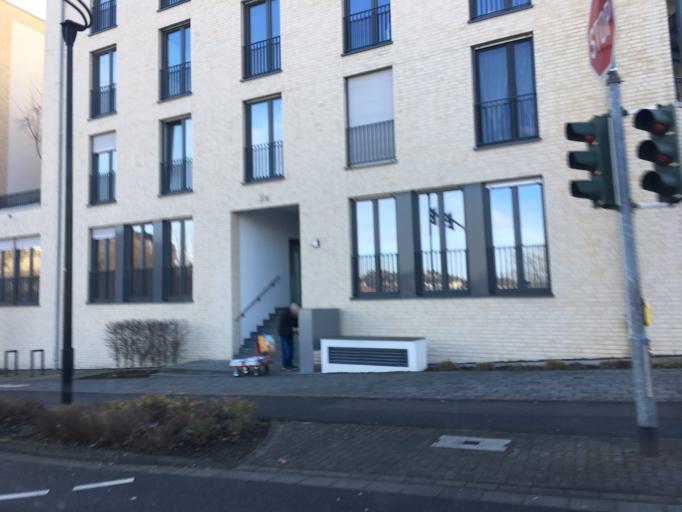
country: DE
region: North Rhine-Westphalia
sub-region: Regierungsbezirk Koln
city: Hurth
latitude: 50.8783
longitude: 6.8793
